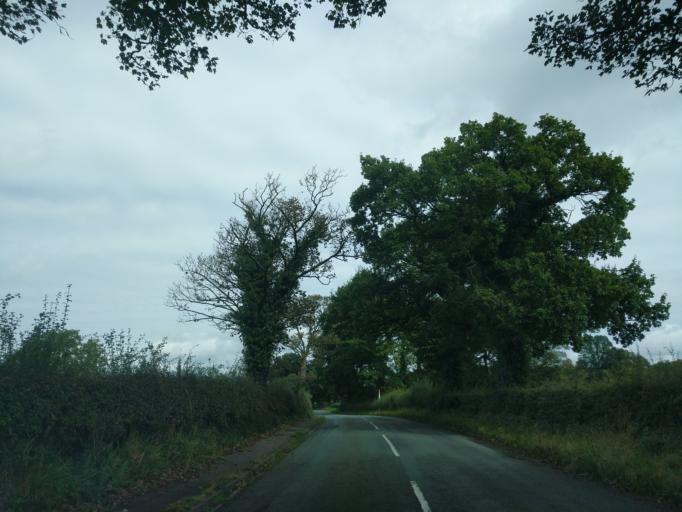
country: GB
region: England
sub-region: Staffordshire
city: Audley
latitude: 53.0004
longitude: -2.2898
